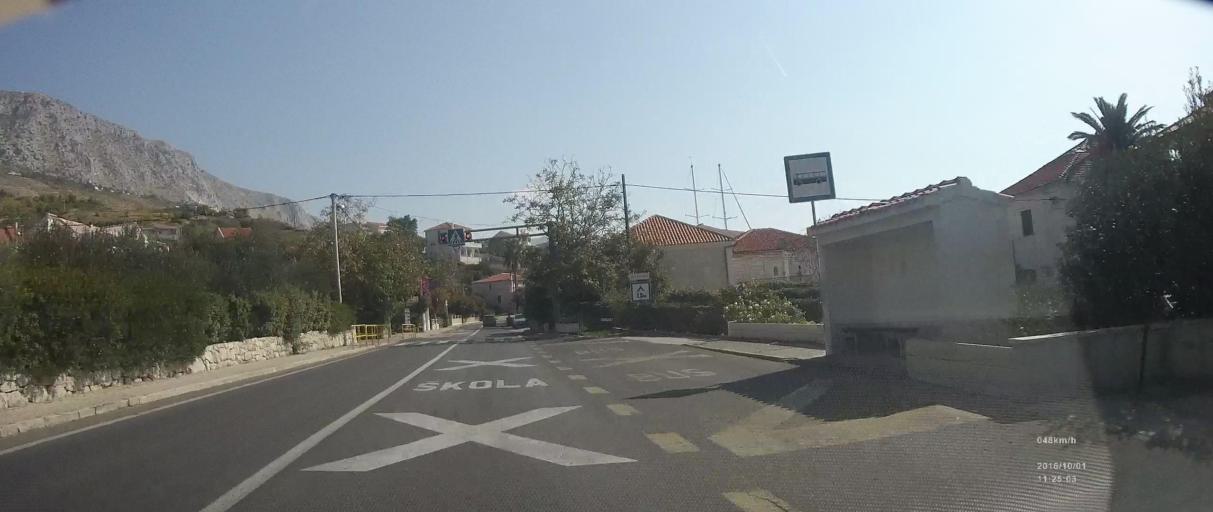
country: HR
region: Splitsko-Dalmatinska
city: Jesenice
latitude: 43.4463
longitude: 16.6342
